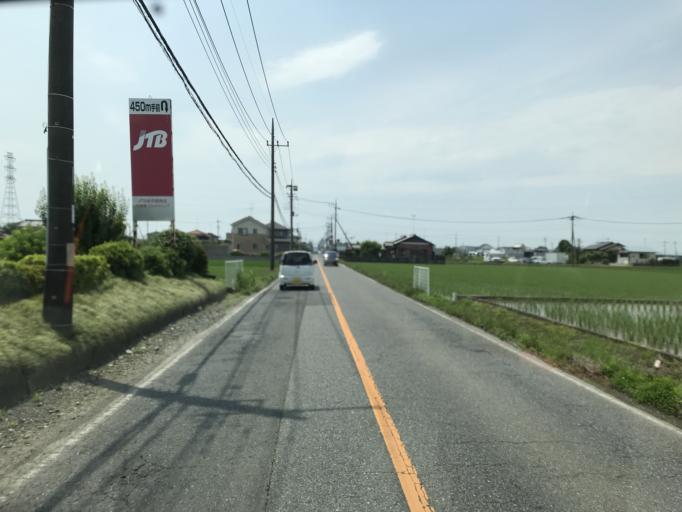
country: JP
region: Saitama
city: Satte
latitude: 36.0769
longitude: 139.7384
